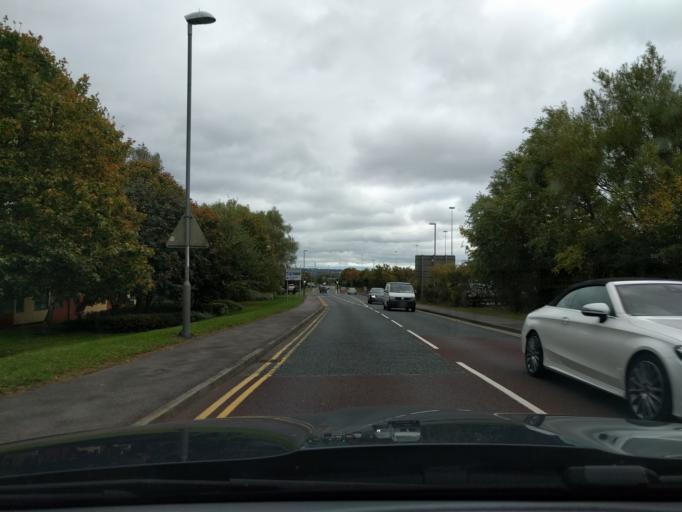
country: GB
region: England
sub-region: Newcastle upon Tyne
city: Benwell
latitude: 54.9621
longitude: -1.6720
